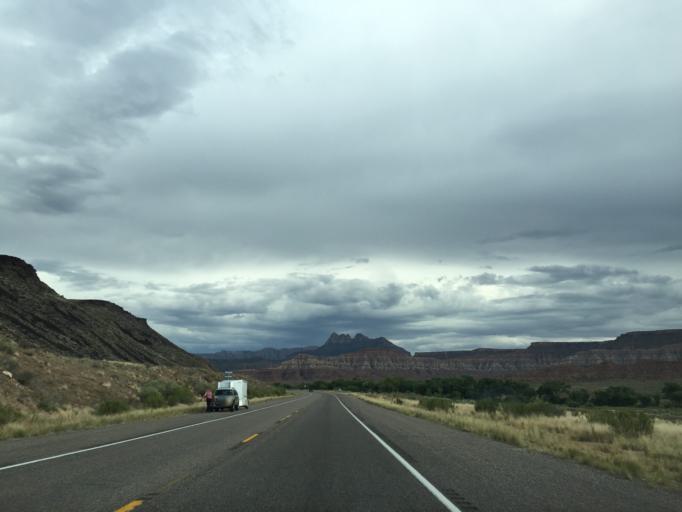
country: US
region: Utah
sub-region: Washington County
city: LaVerkin
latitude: 37.1916
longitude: -113.1435
